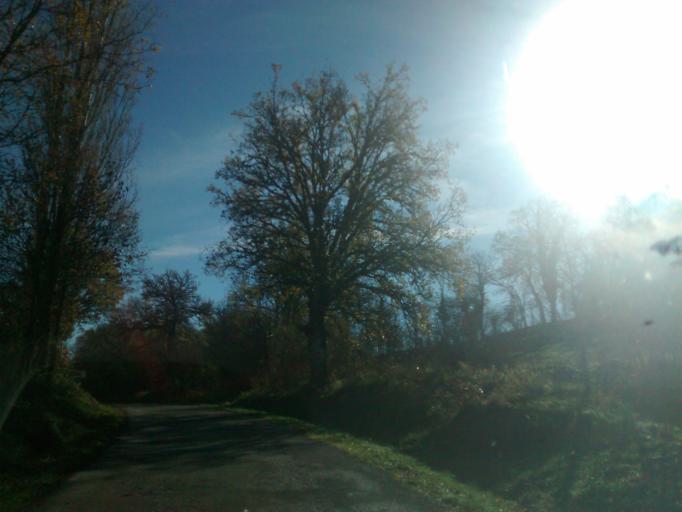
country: ES
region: Cantabria
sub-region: Provincia de Cantabria
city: San Pedro del Romeral
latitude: 42.9704
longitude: -3.7595
